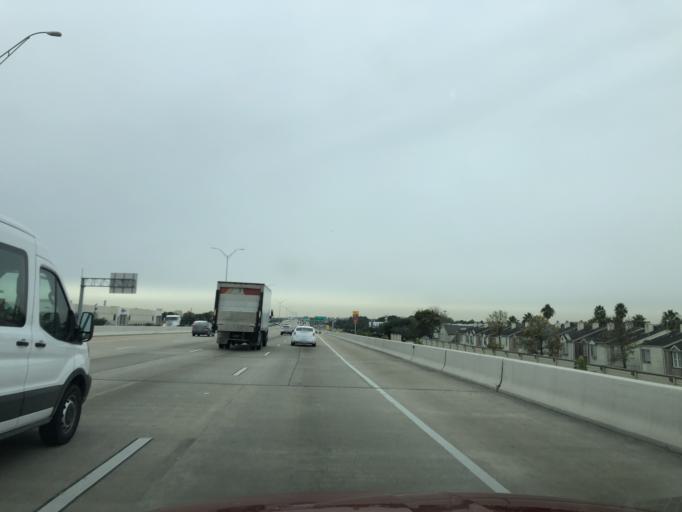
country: US
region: Texas
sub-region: Fort Bend County
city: Missouri City
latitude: 29.6374
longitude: -95.5309
